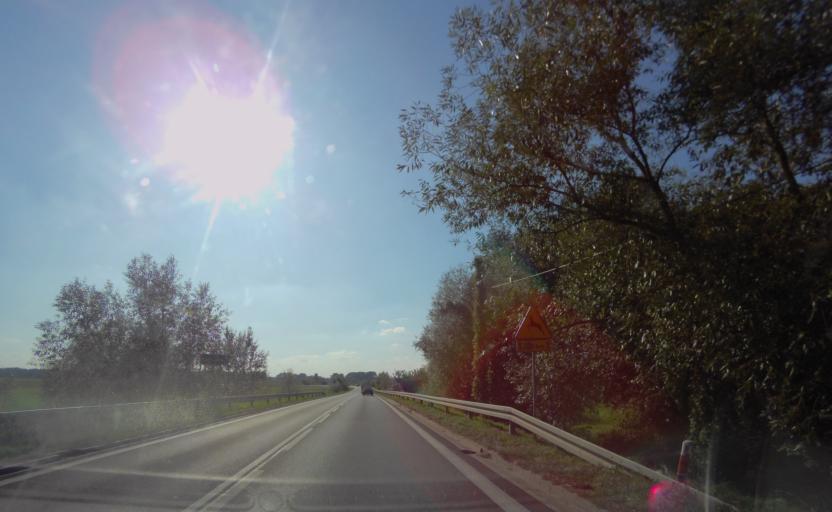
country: PL
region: Subcarpathian Voivodeship
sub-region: Powiat lezajski
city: Kurylowka
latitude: 50.2964
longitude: 22.4582
